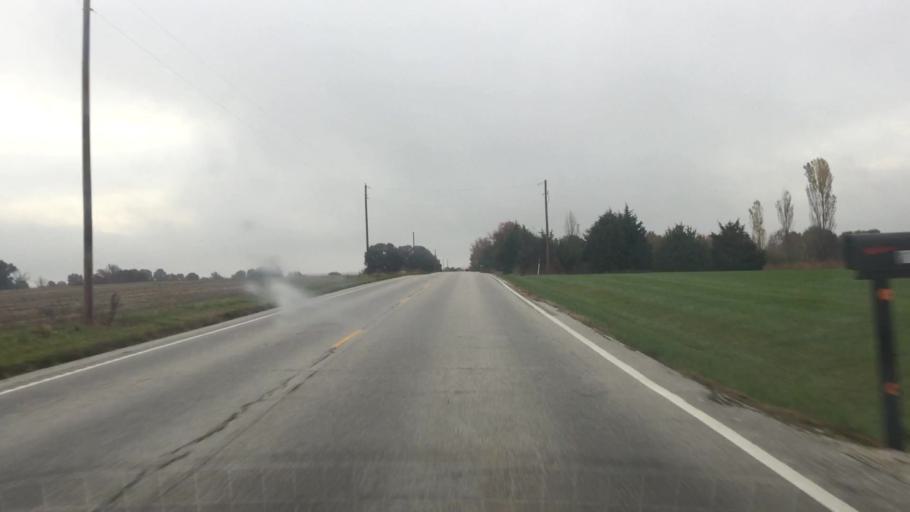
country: US
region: Missouri
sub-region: Boone County
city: Columbia
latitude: 38.9206
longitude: -92.1985
